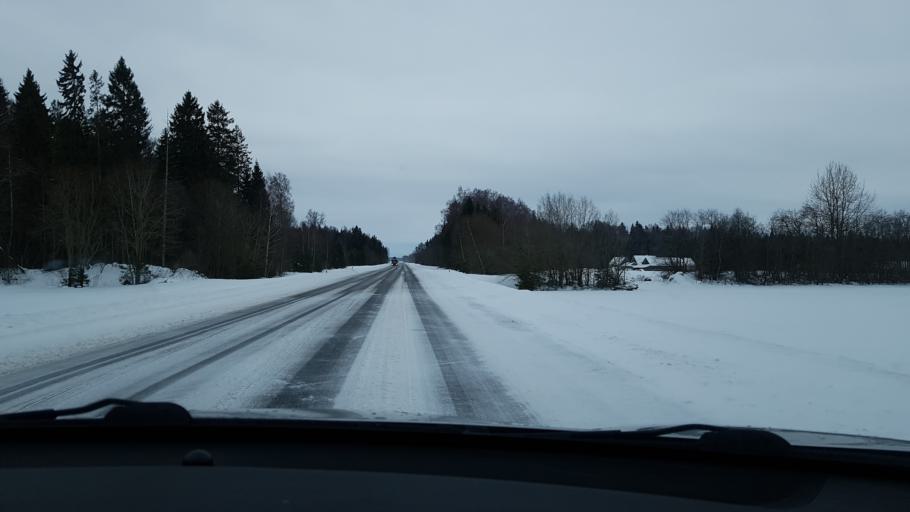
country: EE
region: Jaervamaa
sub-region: Jaerva-Jaani vald
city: Jarva-Jaani
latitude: 59.1357
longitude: 25.7742
